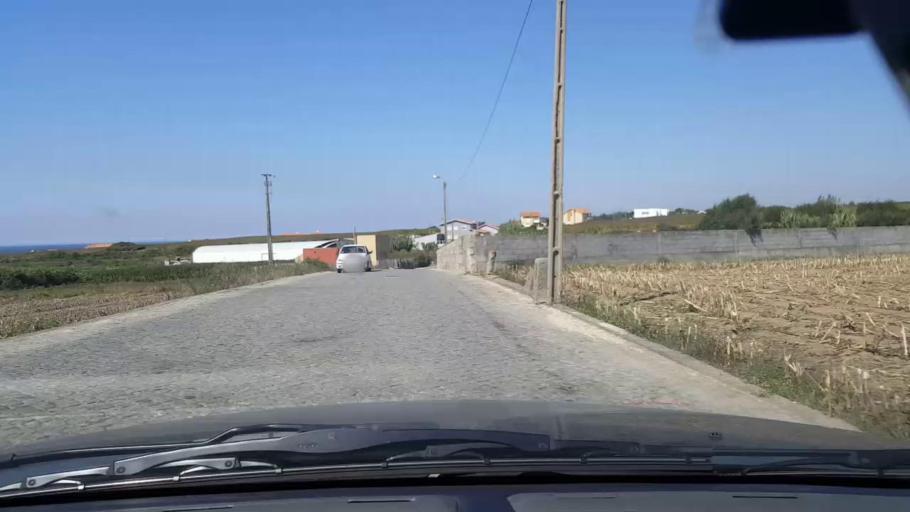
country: PT
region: Porto
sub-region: Matosinhos
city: Lavra
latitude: 41.2863
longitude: -8.7253
